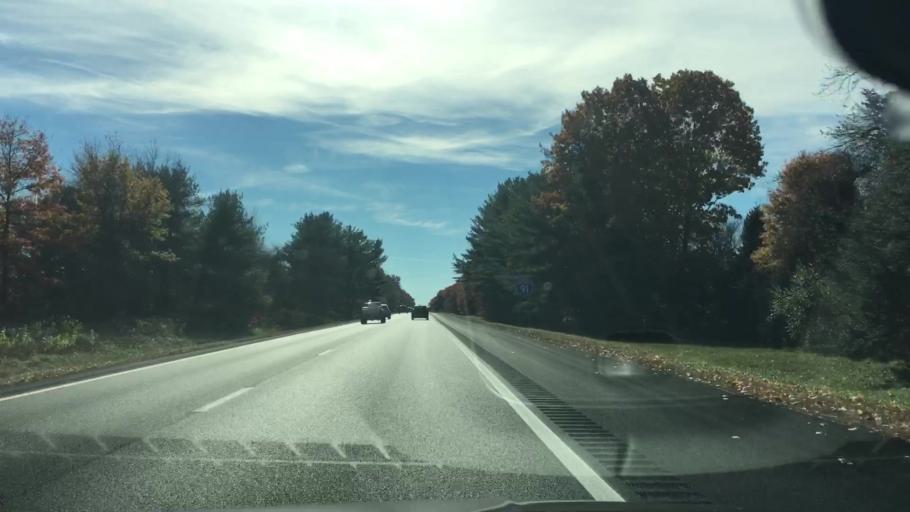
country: US
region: Massachusetts
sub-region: Franklin County
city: Whately
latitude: 42.4304
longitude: -72.6228
